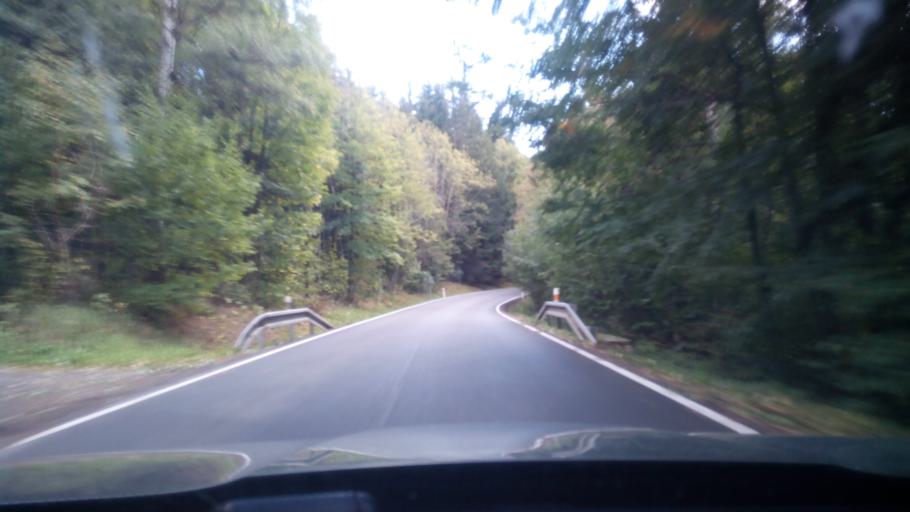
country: CZ
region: Plzensky
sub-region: Okres Klatovy
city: Kasperske Hory
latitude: 49.1397
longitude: 13.6063
